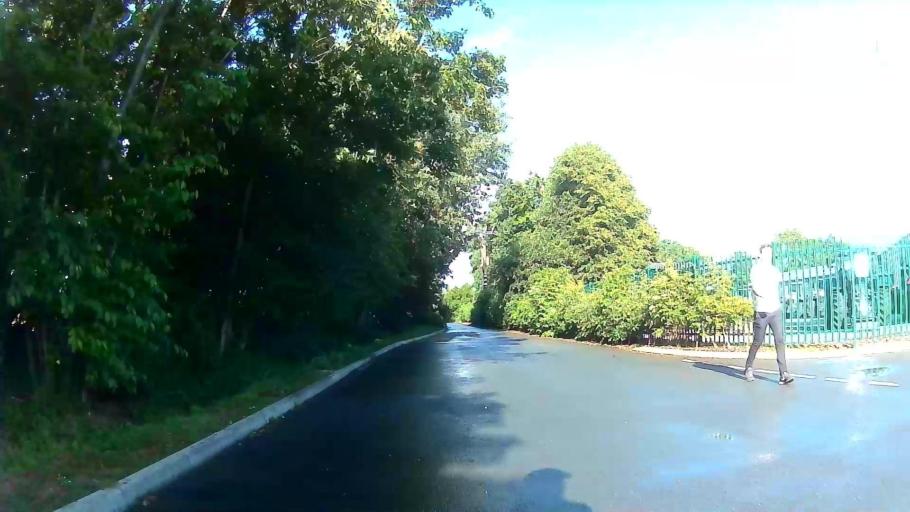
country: GB
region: England
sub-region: Essex
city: Writtle
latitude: 51.7358
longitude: 0.4309
